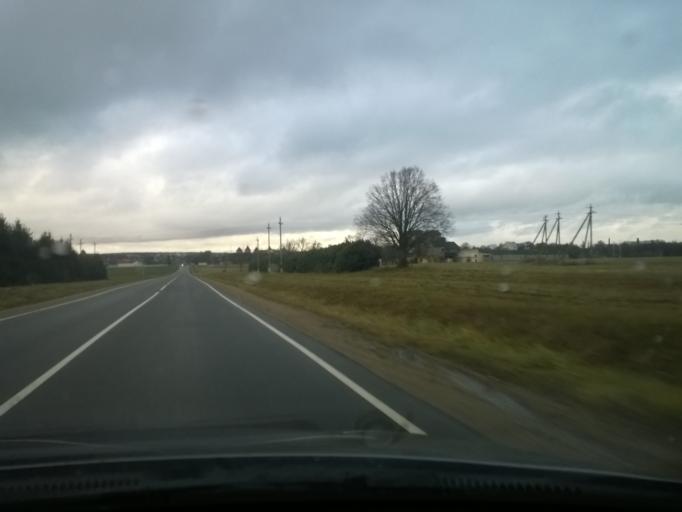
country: BY
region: Grodnenskaya
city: Mir
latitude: 53.4419
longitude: 26.4775
